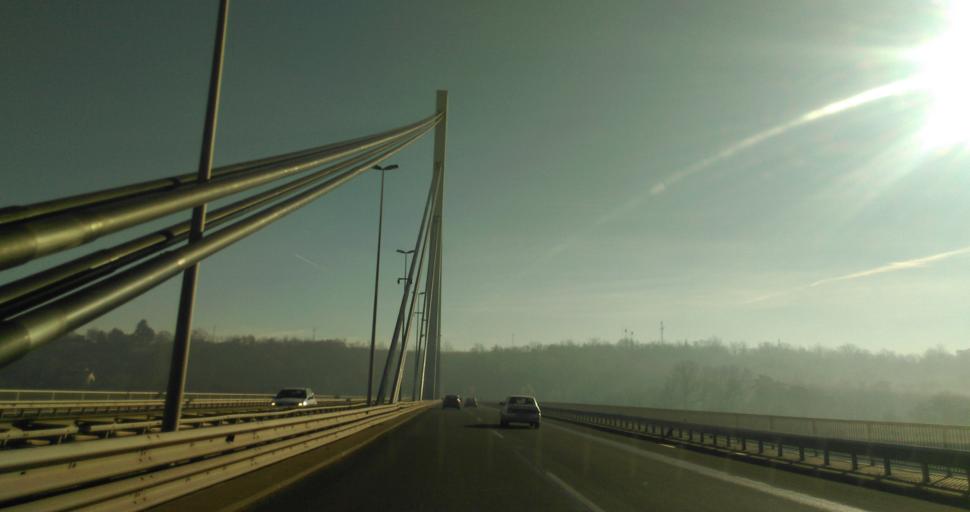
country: RS
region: Autonomna Pokrajina Vojvodina
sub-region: Juznobacki Okrug
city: Novi Sad
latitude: 45.2332
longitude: 19.8504
